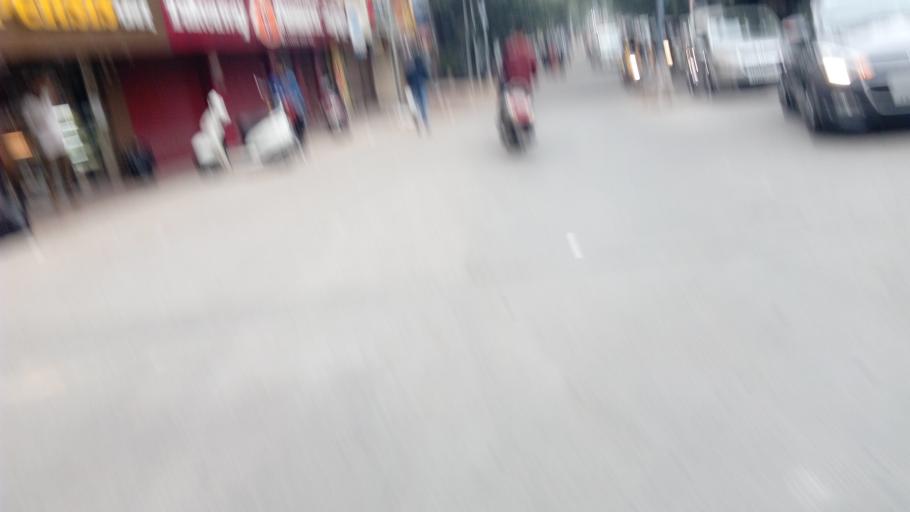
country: IN
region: Telangana
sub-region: Rangareddi
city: Kukatpalli
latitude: 17.4425
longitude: 78.4485
